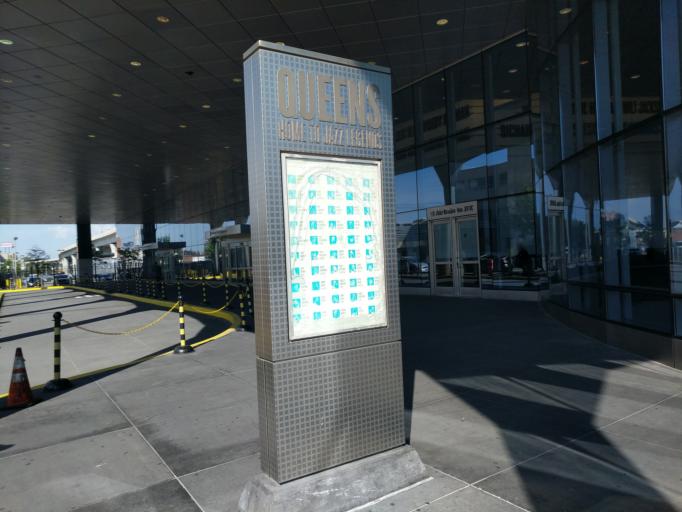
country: US
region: New York
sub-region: Queens County
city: Jamaica
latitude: 40.6990
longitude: -73.8073
